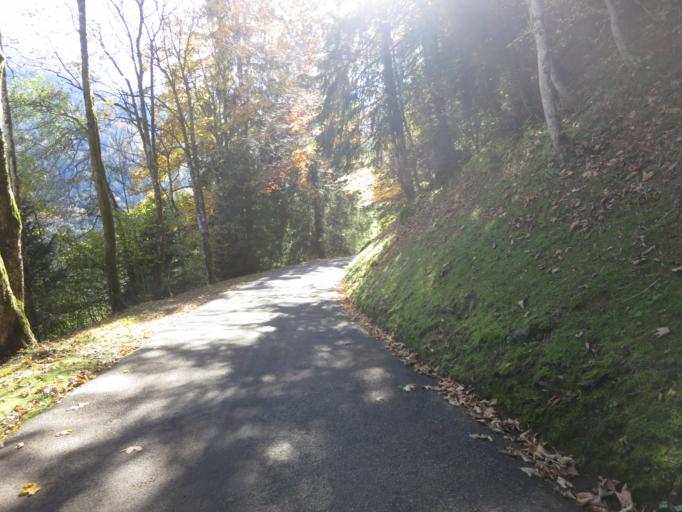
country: CH
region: Schwyz
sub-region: Bezirk March
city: Vorderthal
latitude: 47.0751
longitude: 8.9125
